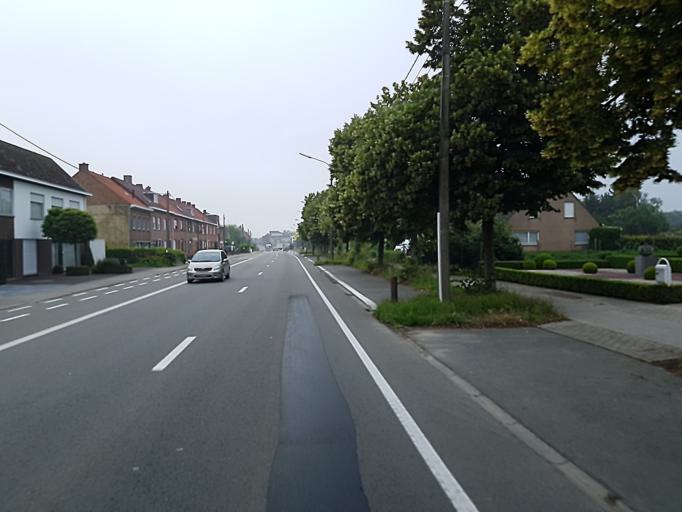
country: BE
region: Flanders
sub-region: Provincie West-Vlaanderen
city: Wevelgem
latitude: 50.7788
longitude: 3.1678
